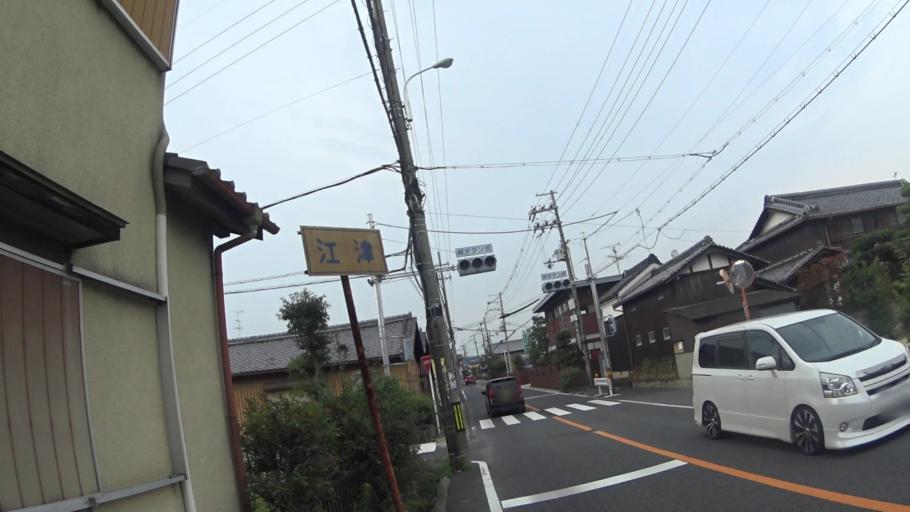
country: JP
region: Kyoto
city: Tanabe
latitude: 34.7897
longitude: 135.7862
